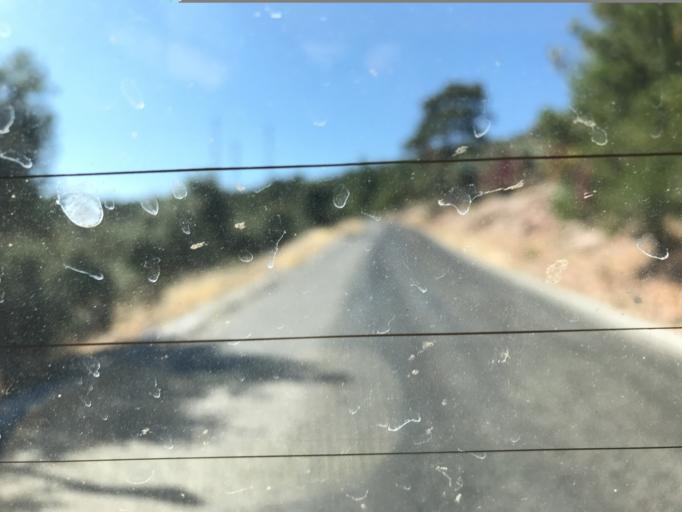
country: TR
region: Mugla
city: Selimiye
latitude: 37.3858
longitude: 27.4833
